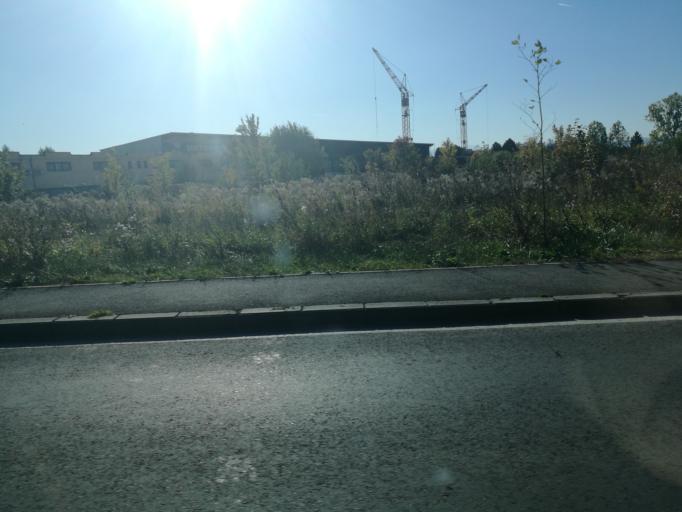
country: RO
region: Brasov
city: Brasov
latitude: 45.6770
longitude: 25.5880
